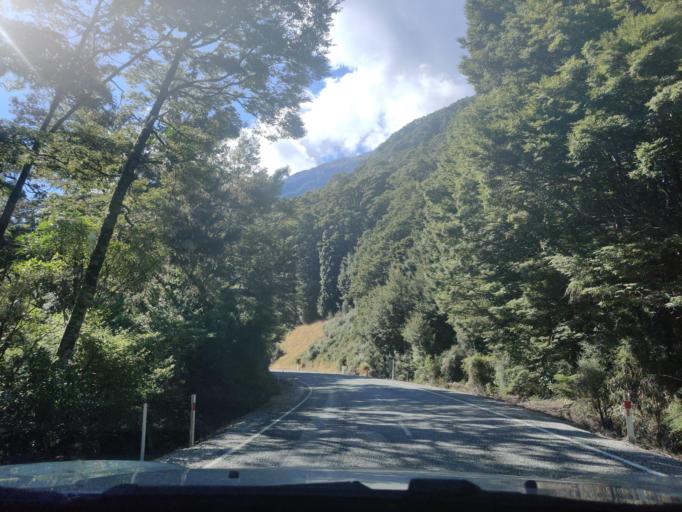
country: NZ
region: Otago
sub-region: Queenstown-Lakes District
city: Wanaka
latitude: -44.1491
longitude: 169.3130
